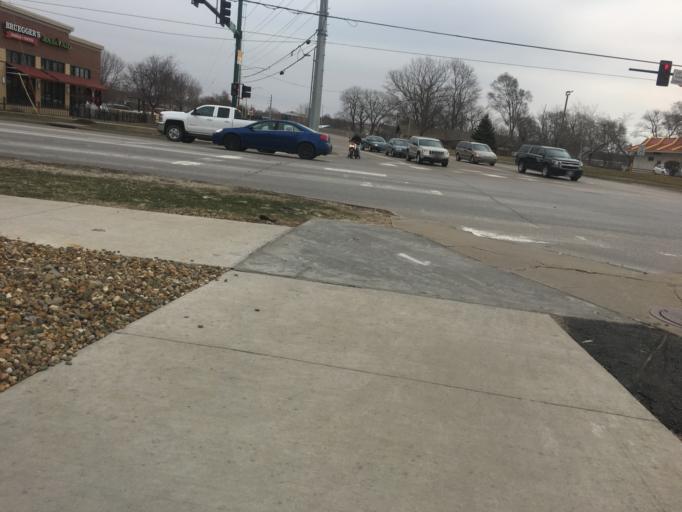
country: US
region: Iowa
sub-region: Johnson County
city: Iowa City
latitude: 41.6506
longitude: -91.5401
